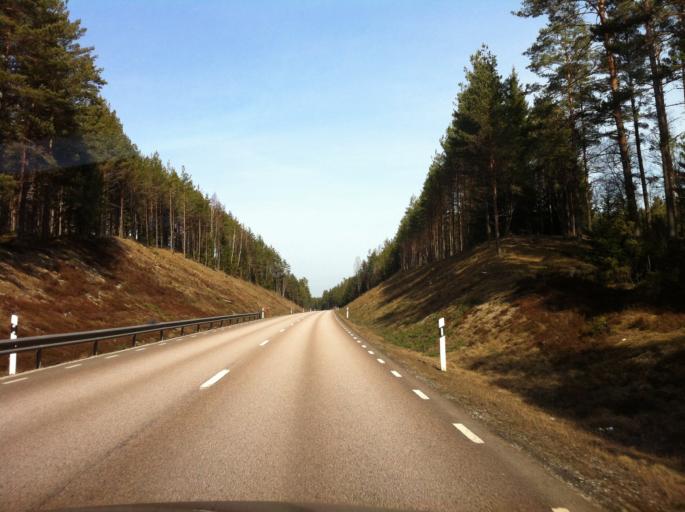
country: SE
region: Joenkoeping
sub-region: Mullsjo Kommun
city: Mullsjoe
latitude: 58.0502
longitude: 13.8514
